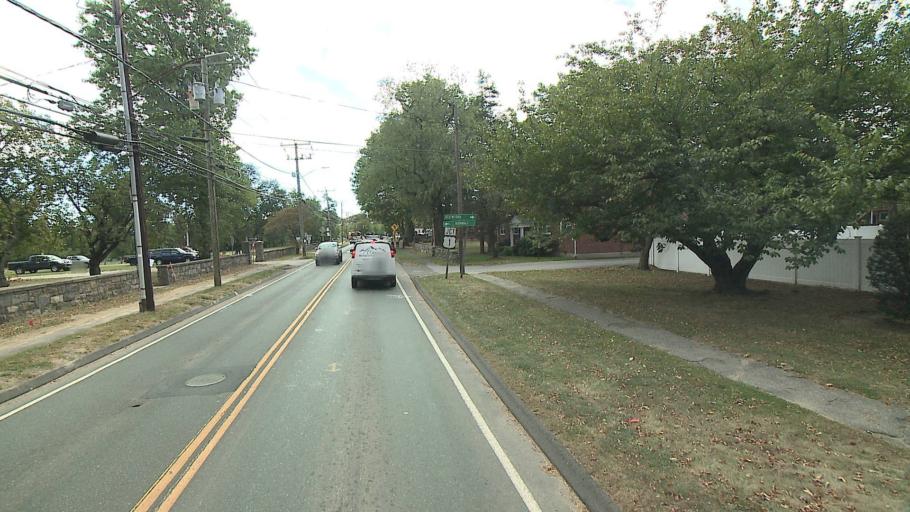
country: US
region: Connecticut
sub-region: Fairfield County
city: Stamford
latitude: 41.0599
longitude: -73.5140
